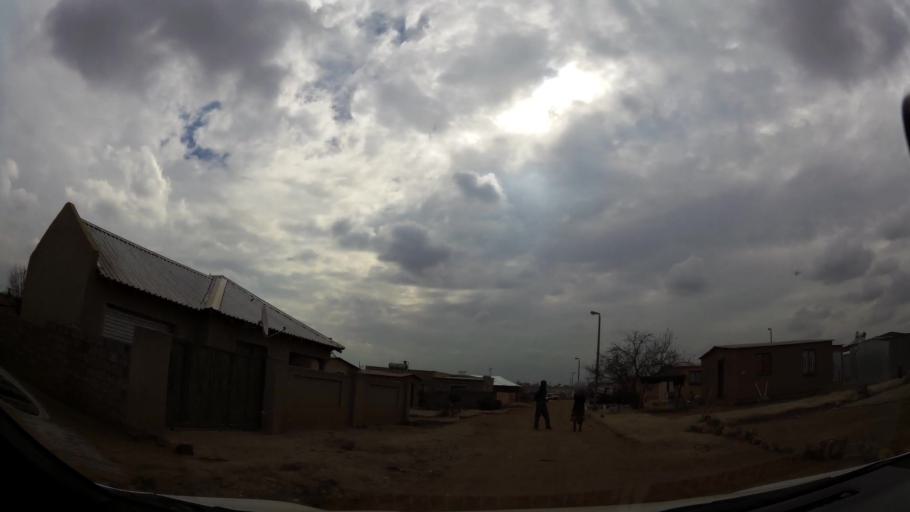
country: ZA
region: Gauteng
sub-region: Ekurhuleni Metropolitan Municipality
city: Germiston
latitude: -26.3789
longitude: 28.1165
